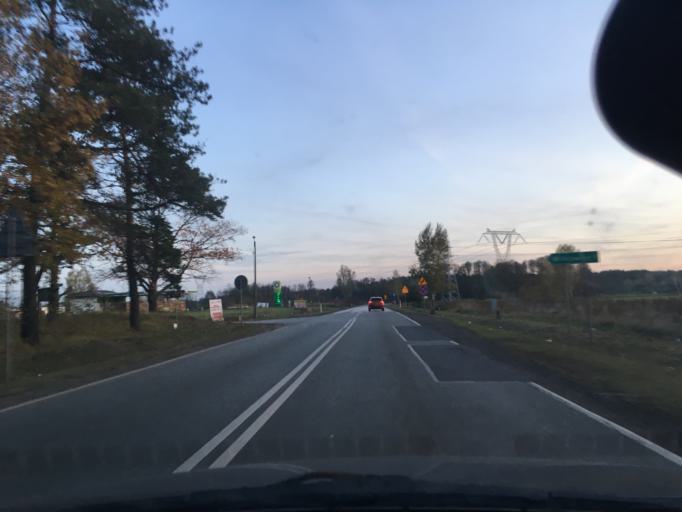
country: PL
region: Masovian Voivodeship
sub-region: Powiat sochaczewski
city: Mlodzieszyn
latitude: 52.3357
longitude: 20.2155
